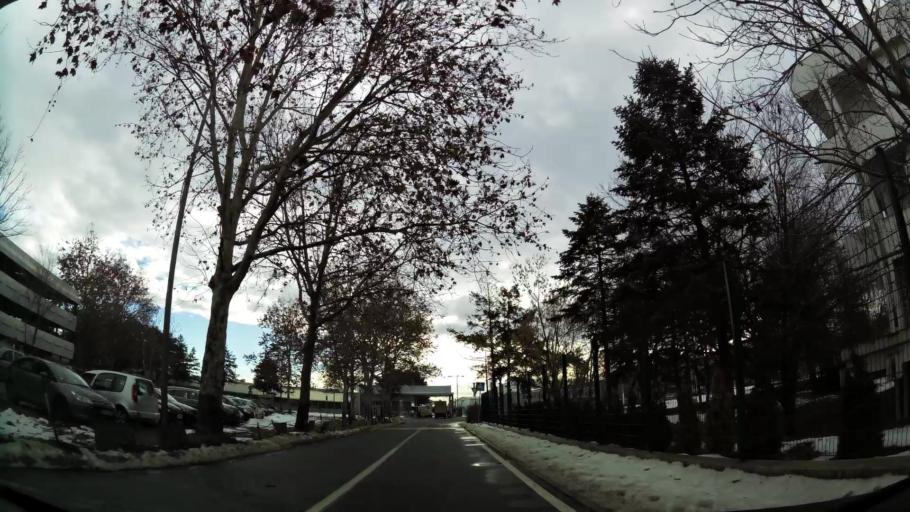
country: RS
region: Central Serbia
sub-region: Belgrade
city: Surcin
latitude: 44.8182
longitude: 20.2882
